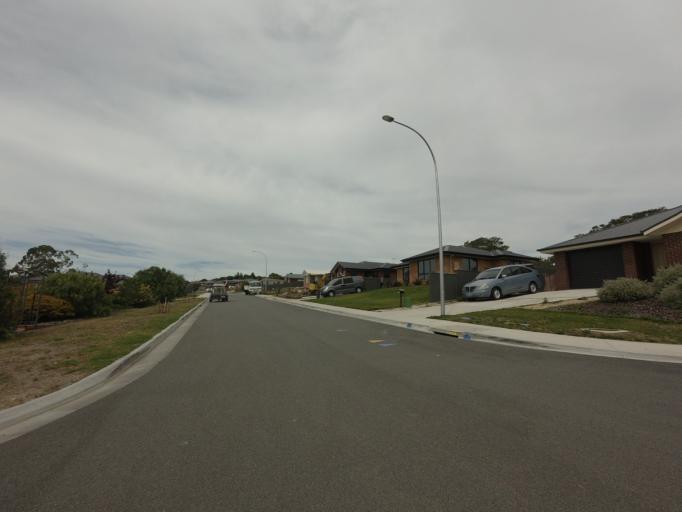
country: AU
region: Tasmania
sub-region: Sorell
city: Sorell
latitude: -42.7911
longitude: 147.5294
